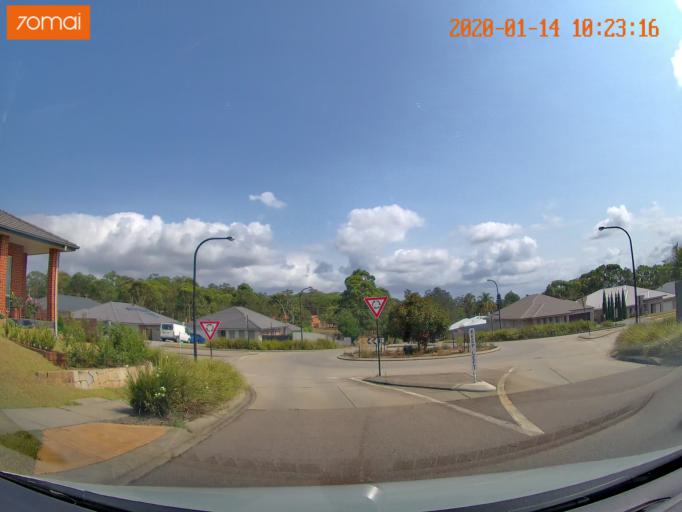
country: AU
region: New South Wales
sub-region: Lake Macquarie Shire
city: Dora Creek
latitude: -33.1093
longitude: 151.5094
